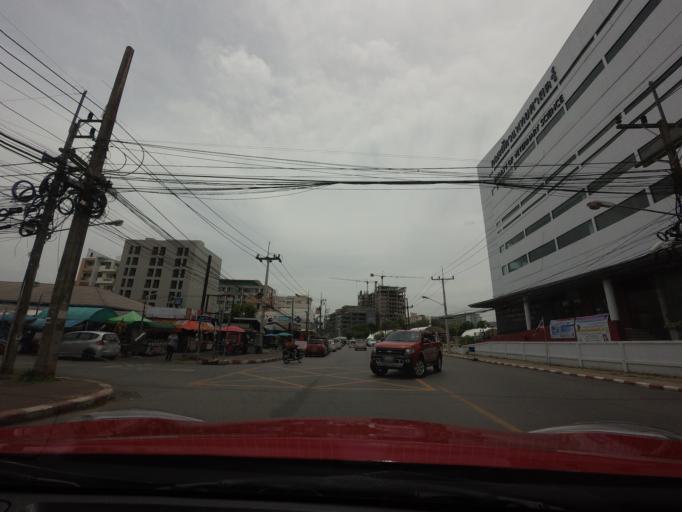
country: TH
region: Songkhla
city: Hat Yai
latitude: 7.0016
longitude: 100.5014
